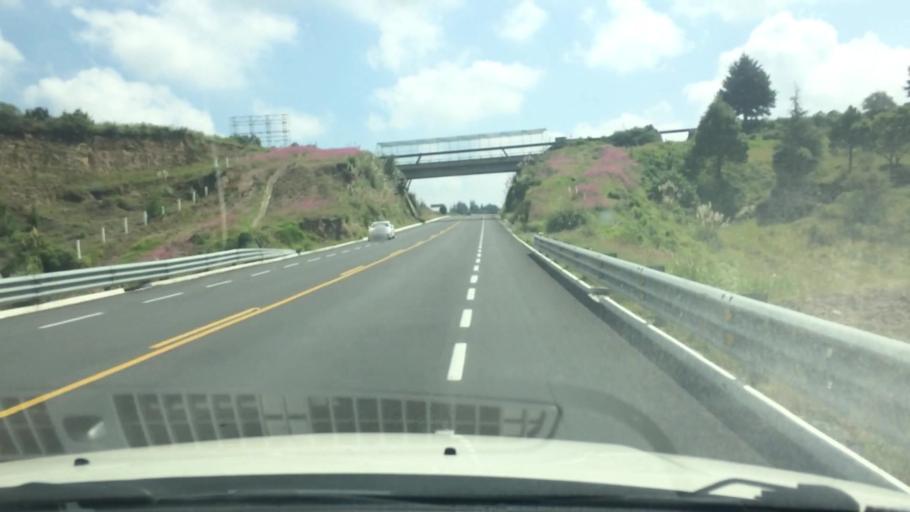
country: MX
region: Mexico
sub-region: Villa Victoria
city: Colonia Doctor Gustavo Baz
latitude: 19.3770
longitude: -99.8851
